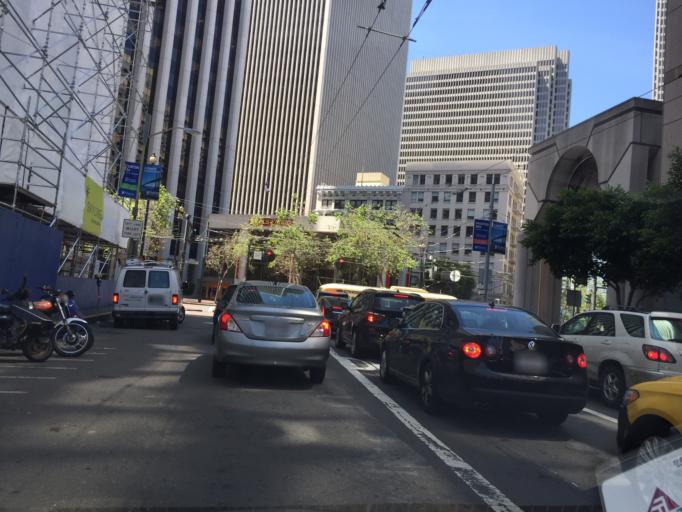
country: US
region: California
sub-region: San Francisco County
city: San Francisco
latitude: 37.7927
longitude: -122.3960
